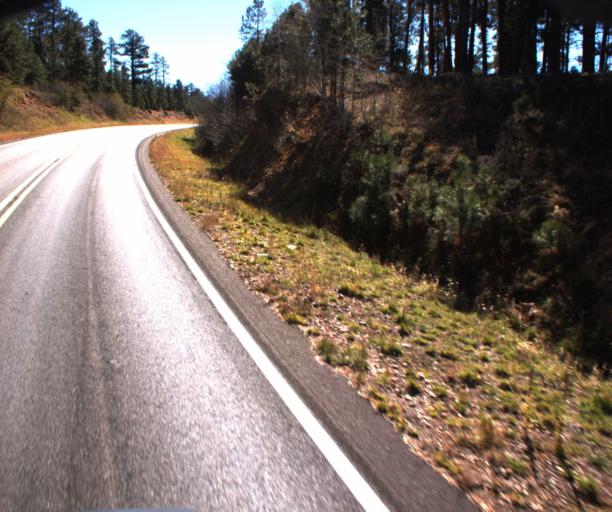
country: US
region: Arizona
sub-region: Coconino County
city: Fredonia
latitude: 36.7029
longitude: -112.2171
